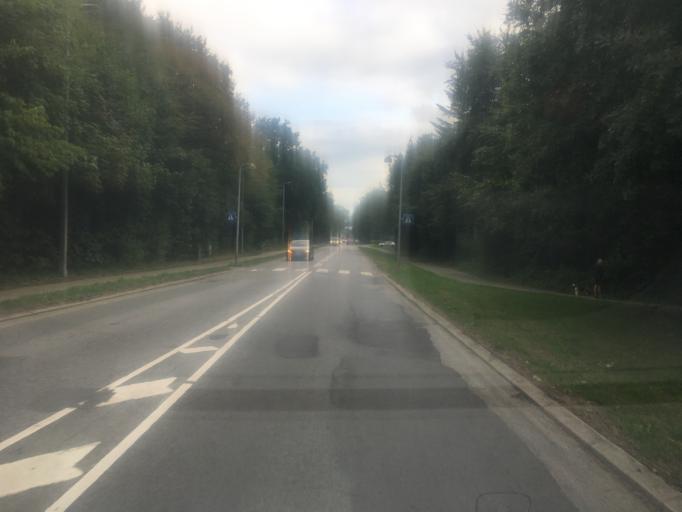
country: DK
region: South Denmark
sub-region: Tonder Kommune
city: Tonder
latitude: 54.9455
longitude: 8.8554
